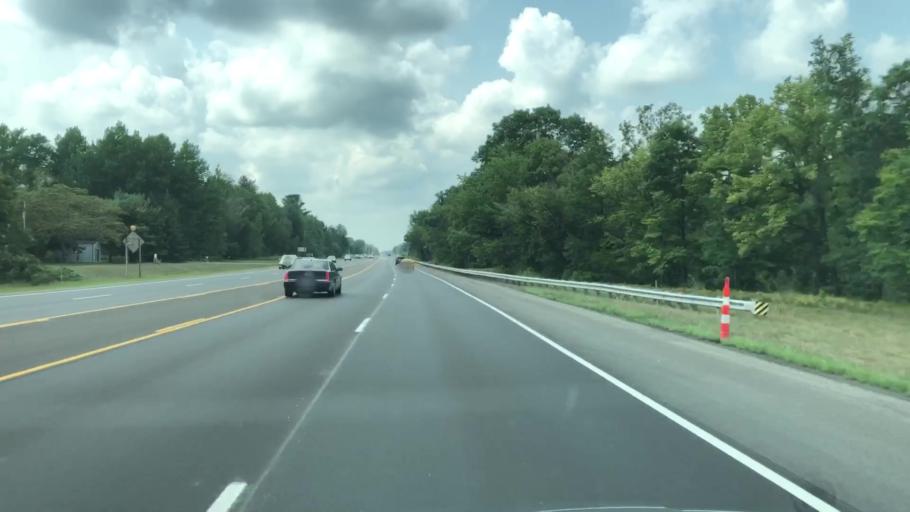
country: US
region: Michigan
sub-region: Isabella County
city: Shepherd
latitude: 43.6114
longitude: -84.5929
